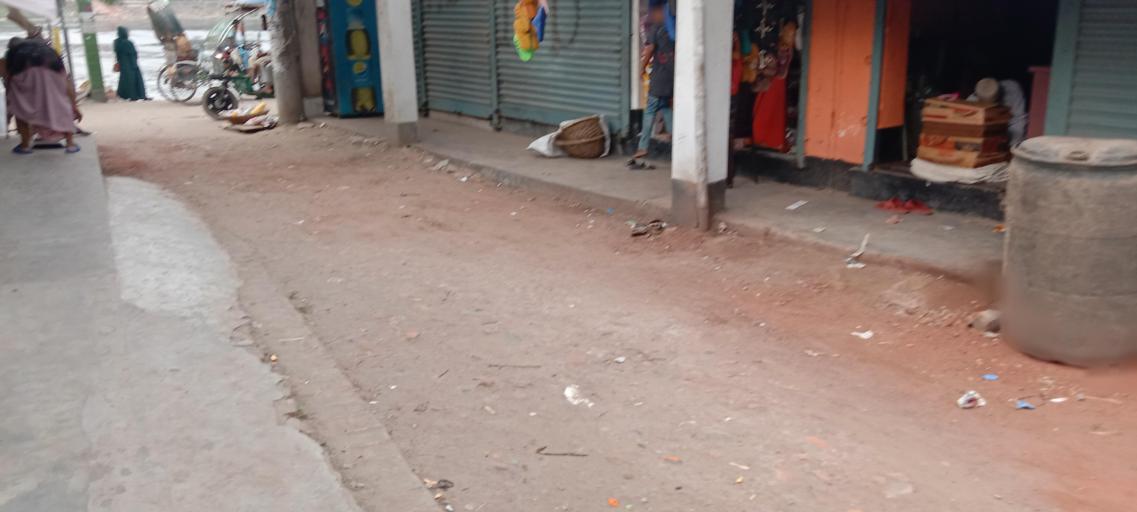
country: BD
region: Dhaka
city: Azimpur
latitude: 23.7059
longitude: 90.3758
